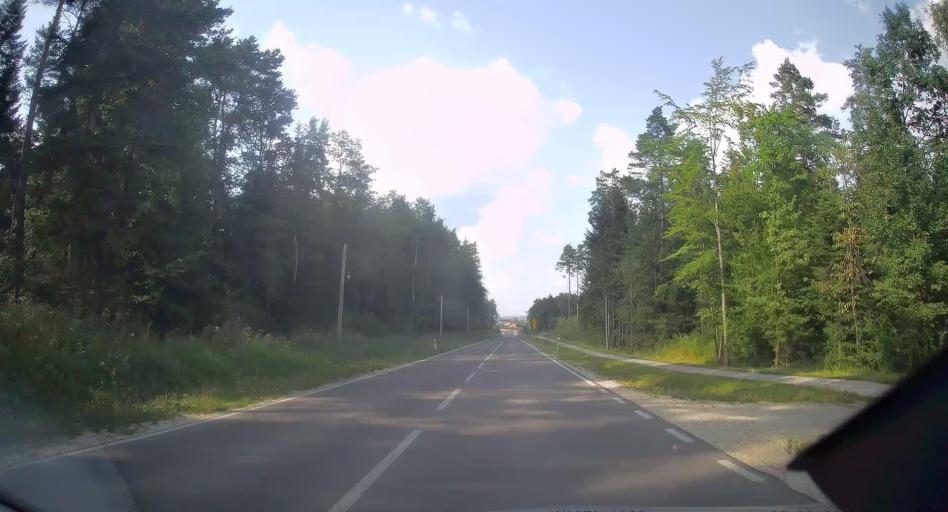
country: PL
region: Swietokrzyskie
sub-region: Powiat konecki
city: Radoszyce
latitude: 51.0221
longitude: 20.2908
